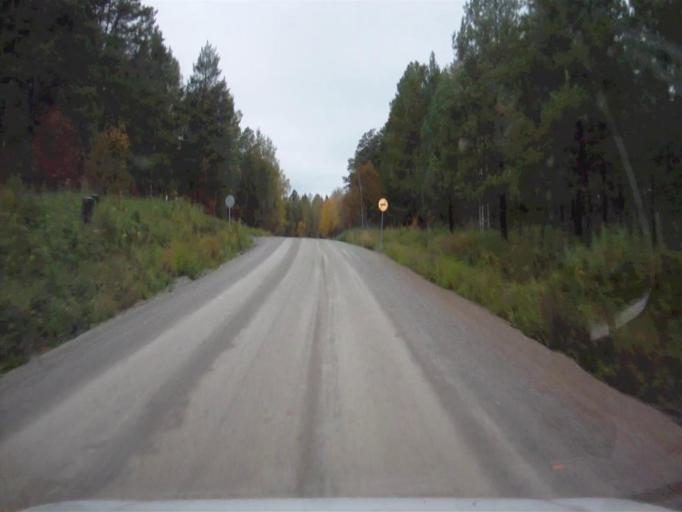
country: RU
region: Chelyabinsk
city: Nyazepetrovsk
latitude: 56.0619
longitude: 59.4479
